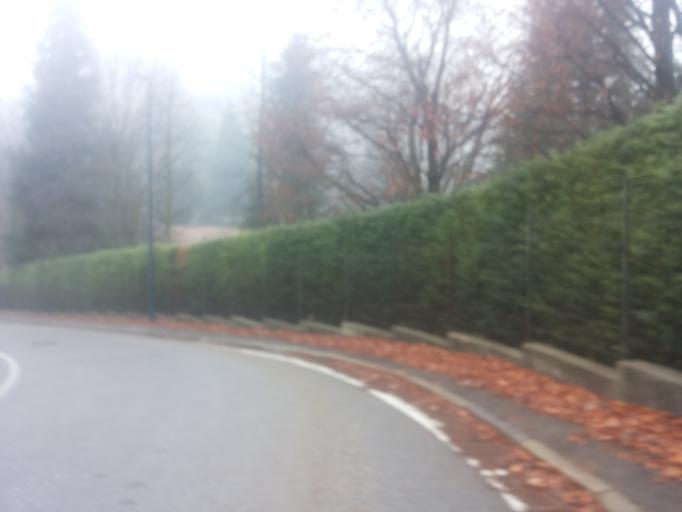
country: IT
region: Piedmont
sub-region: Provincia di Torino
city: Turin
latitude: 45.0483
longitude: 7.7091
